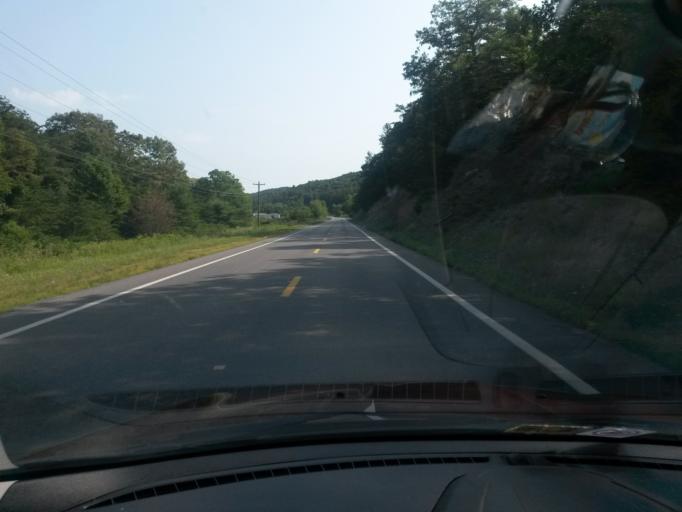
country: US
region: Virginia
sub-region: Shenandoah County
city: Basye
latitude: 38.8237
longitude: -78.8809
